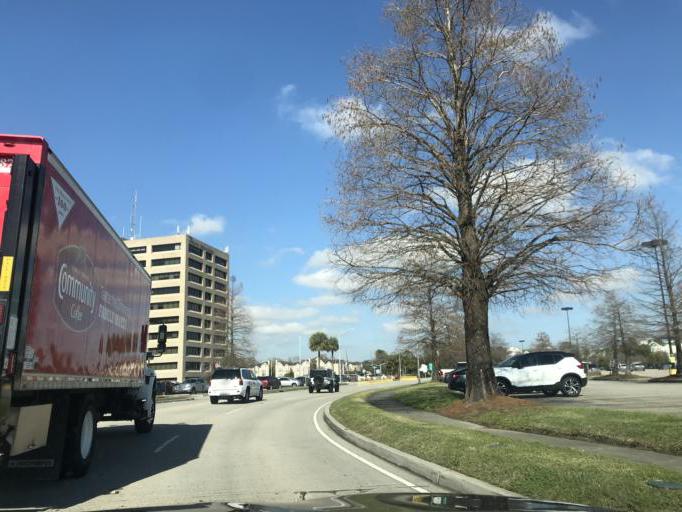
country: US
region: Louisiana
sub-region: Jefferson Parish
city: Elmwood
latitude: 29.9643
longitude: -90.1878
